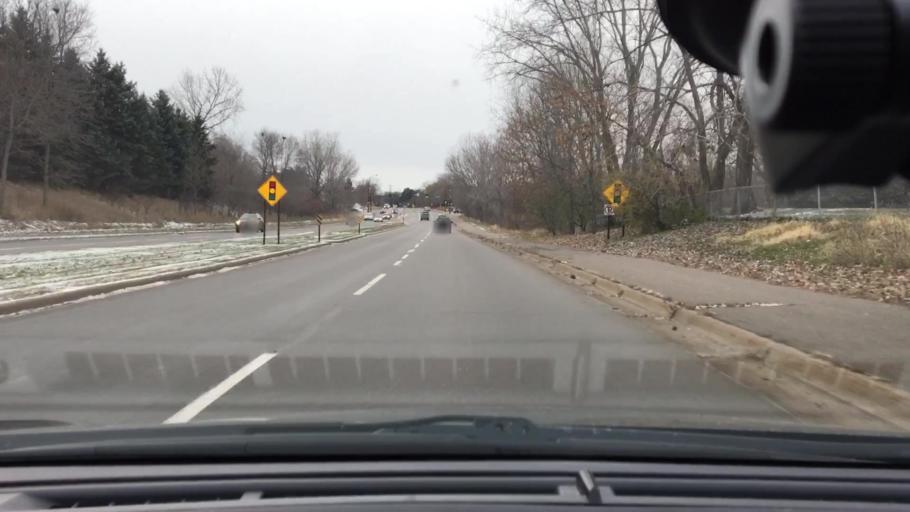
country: US
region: Minnesota
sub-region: Hennepin County
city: Plymouth
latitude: 45.0334
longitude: -93.4306
